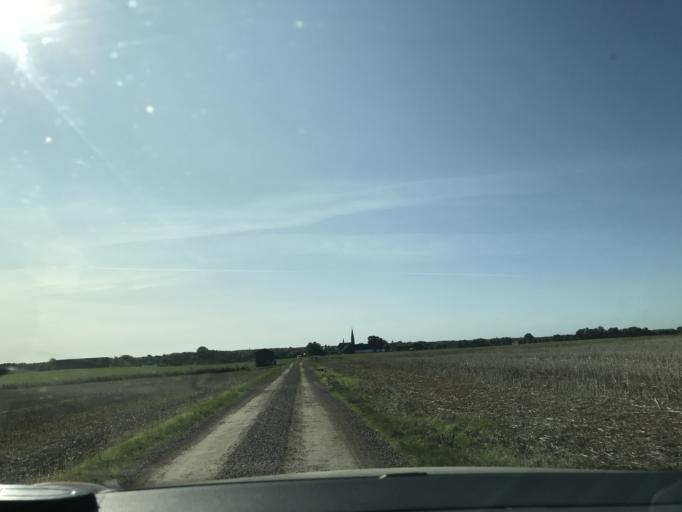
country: SE
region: Skane
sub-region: Landskrona
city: Asmundtorp
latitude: 55.8989
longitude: 12.9490
